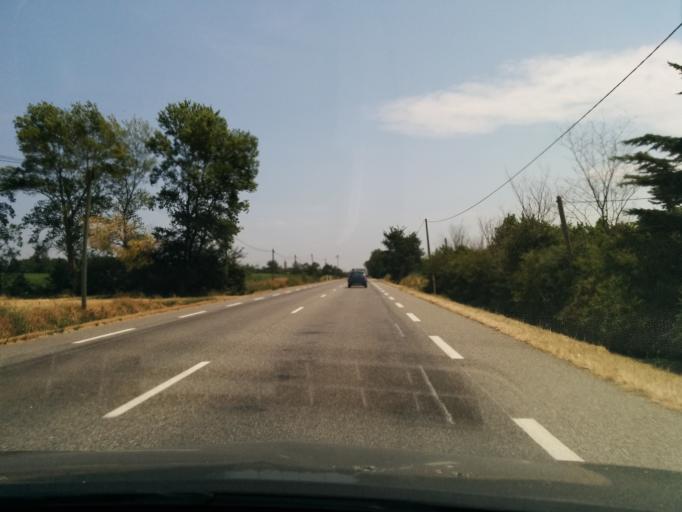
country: FR
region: Midi-Pyrenees
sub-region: Departement de la Haute-Garonne
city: Avignonet-Lauragais
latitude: 43.3754
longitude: 1.7587
